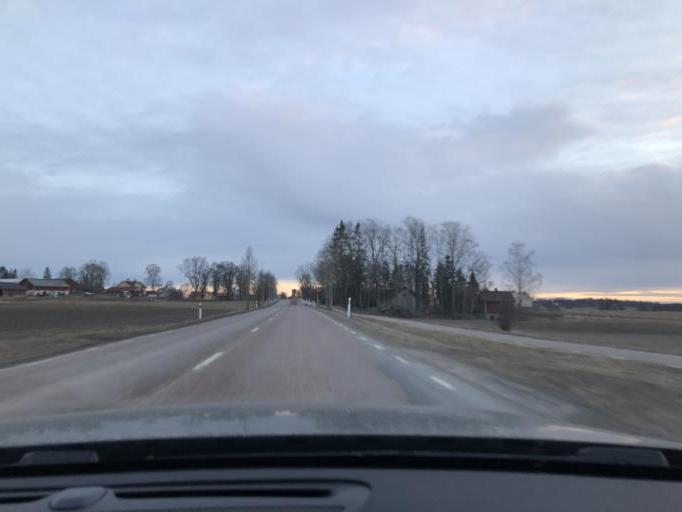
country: SE
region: Uppsala
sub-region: Uppsala Kommun
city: Gamla Uppsala
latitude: 59.9165
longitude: 17.6425
